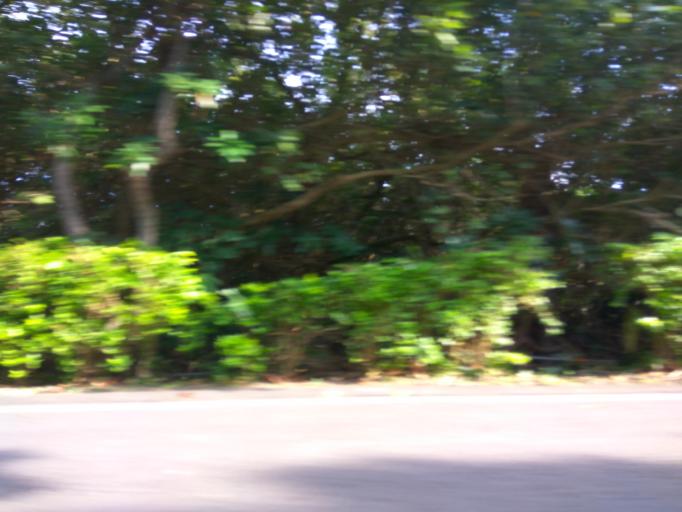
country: TW
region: Taiwan
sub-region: Hsinchu
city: Zhubei
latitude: 24.9417
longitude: 120.9887
